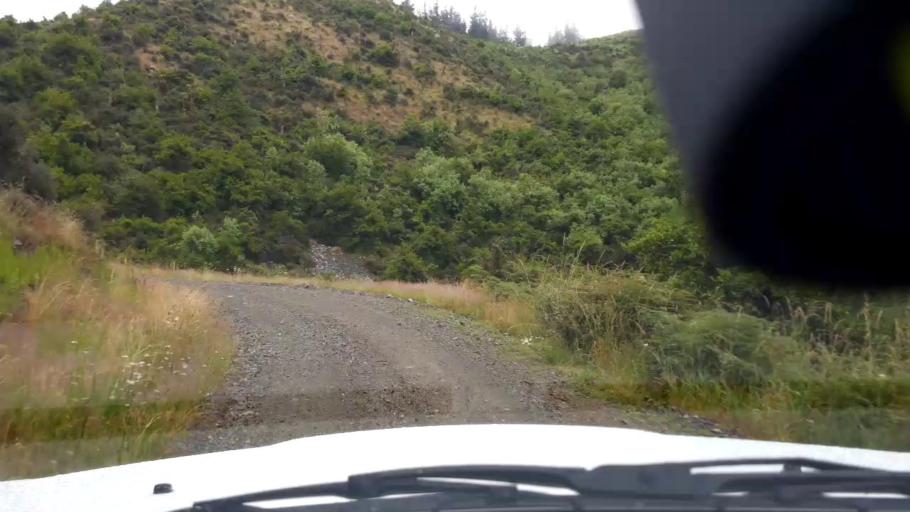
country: NZ
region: Canterbury
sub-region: Timaru District
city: Pleasant Point
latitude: -44.0331
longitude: 170.9957
